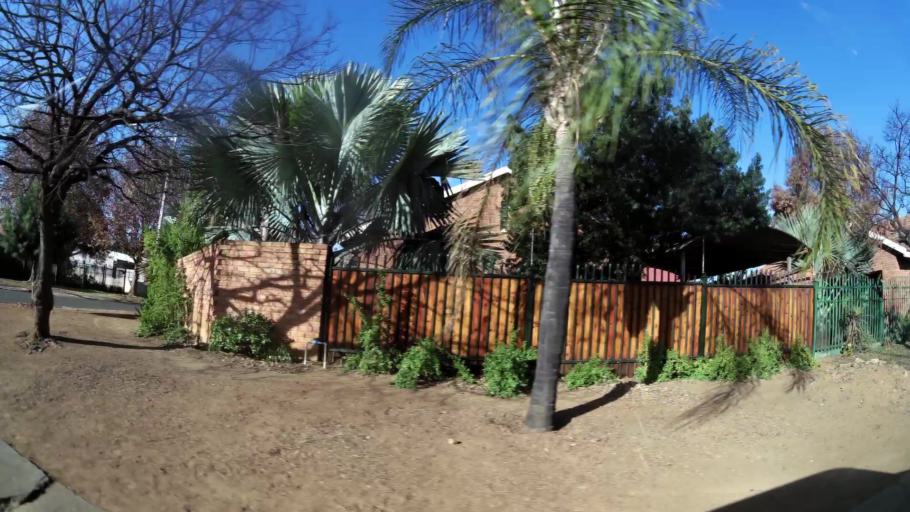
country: ZA
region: Gauteng
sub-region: City of Tshwane Metropolitan Municipality
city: Pretoria
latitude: -25.7126
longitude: 28.2478
